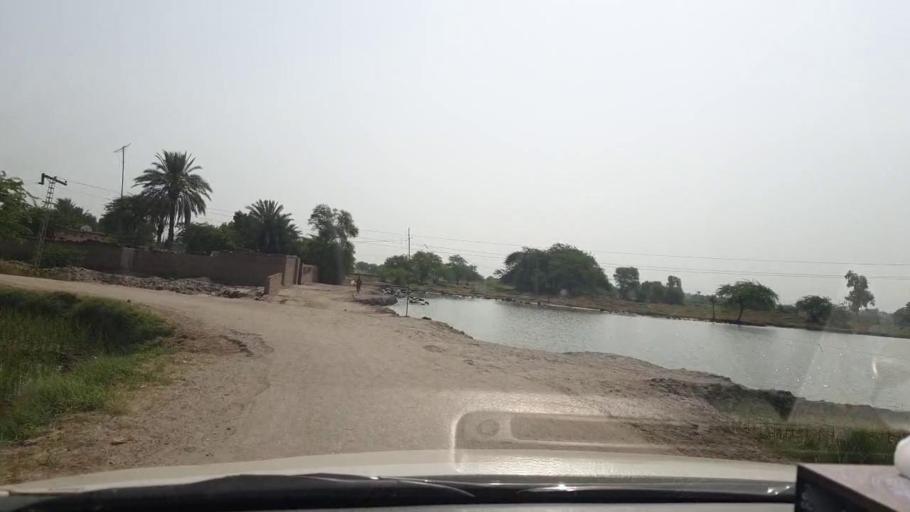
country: PK
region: Sindh
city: Shikarpur
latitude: 27.9809
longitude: 68.6653
